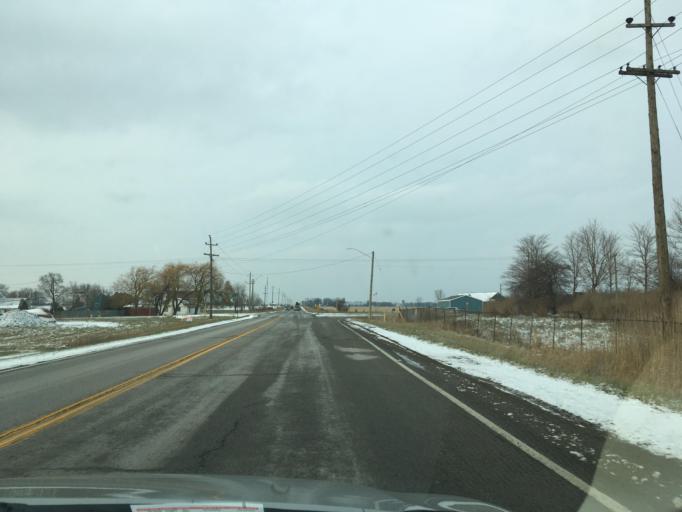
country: CA
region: Ontario
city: Norfolk County
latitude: 42.8112
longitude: -80.0629
